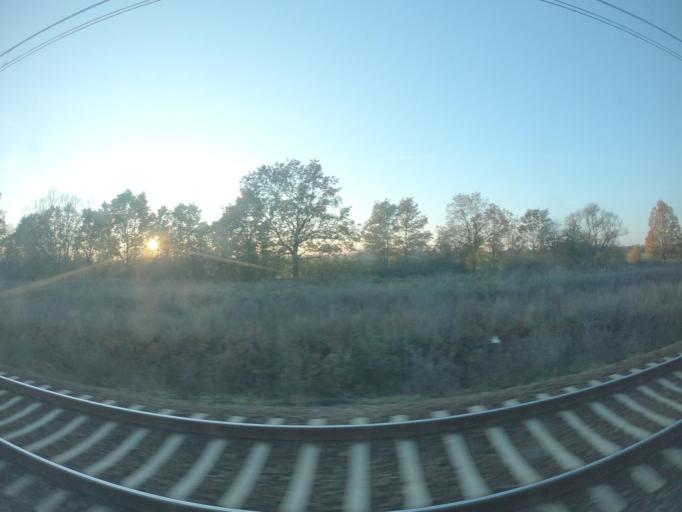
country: PL
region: Lubusz
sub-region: Powiat slubicki
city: Gorzyca
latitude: 52.5288
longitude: 14.6505
